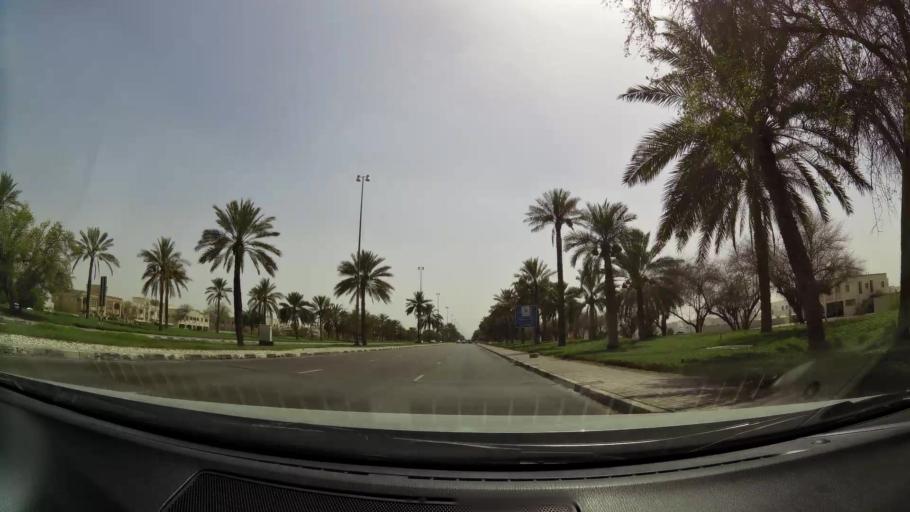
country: AE
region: Abu Dhabi
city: Al Ain
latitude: 24.2211
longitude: 55.6947
